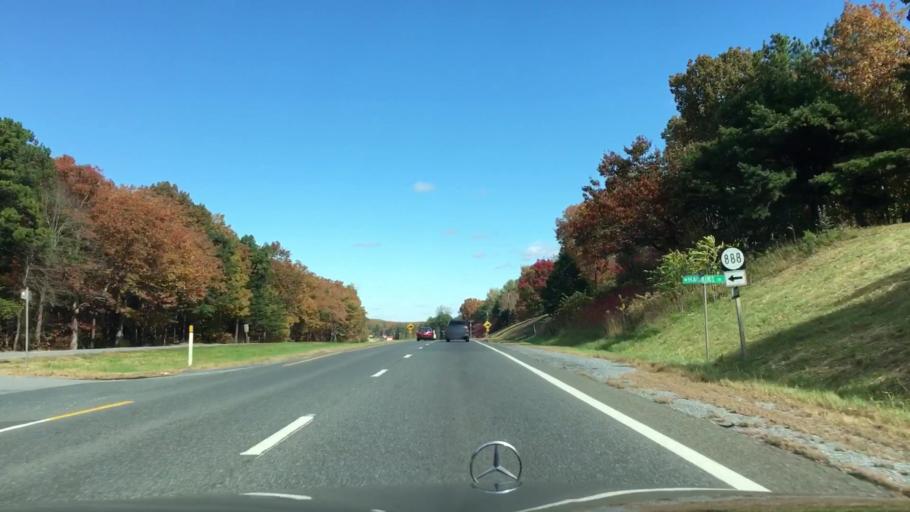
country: US
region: Virginia
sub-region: Campbell County
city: Rustburg
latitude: 37.2203
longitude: -79.1925
